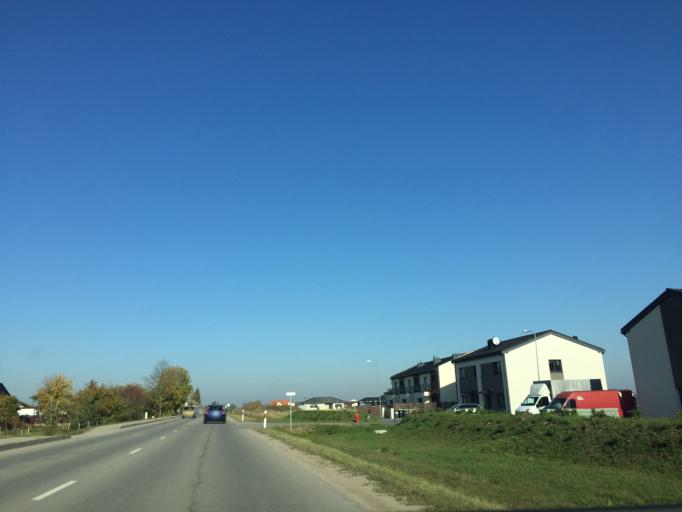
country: LT
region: Klaipedos apskritis
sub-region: Klaipeda
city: Klaipeda
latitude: 55.7402
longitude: 21.1926
